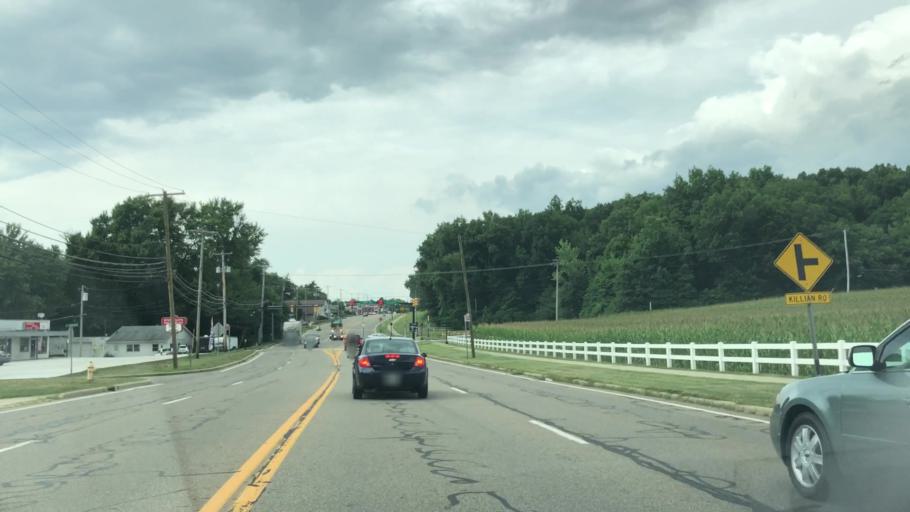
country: US
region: Ohio
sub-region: Summit County
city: Portage Lakes
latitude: 40.9969
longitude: -81.5232
